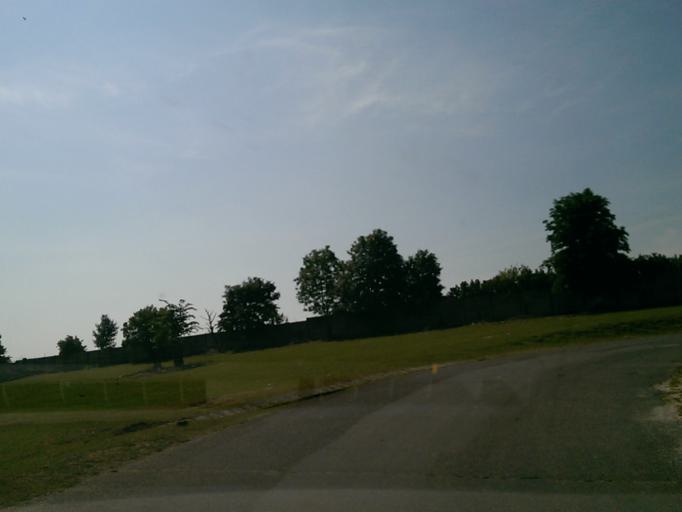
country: CZ
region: Kralovehradecky
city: Dvur Kralove nad Labem
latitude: 50.4335
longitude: 15.7801
